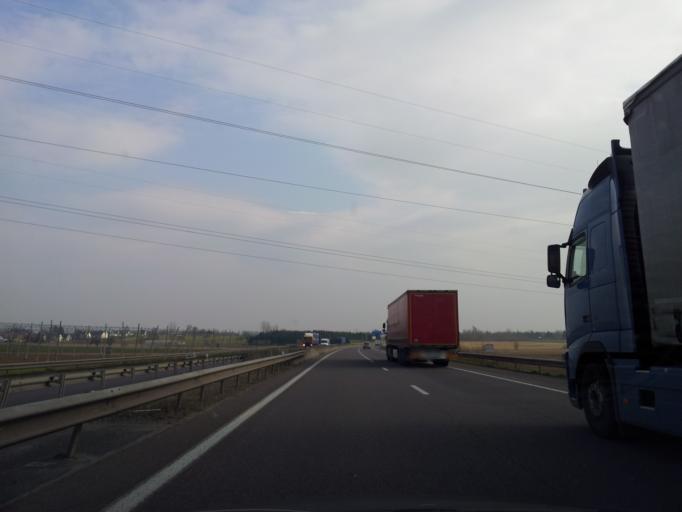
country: FR
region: Alsace
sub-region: Departement du Bas-Rhin
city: Mommenheim
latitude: 48.7544
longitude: 7.6761
